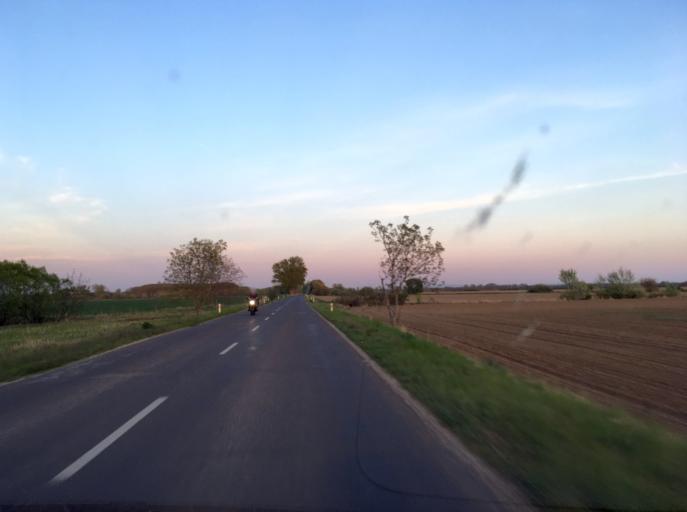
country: SK
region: Nitriansky
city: Kolarovo
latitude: 47.9207
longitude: 18.0369
